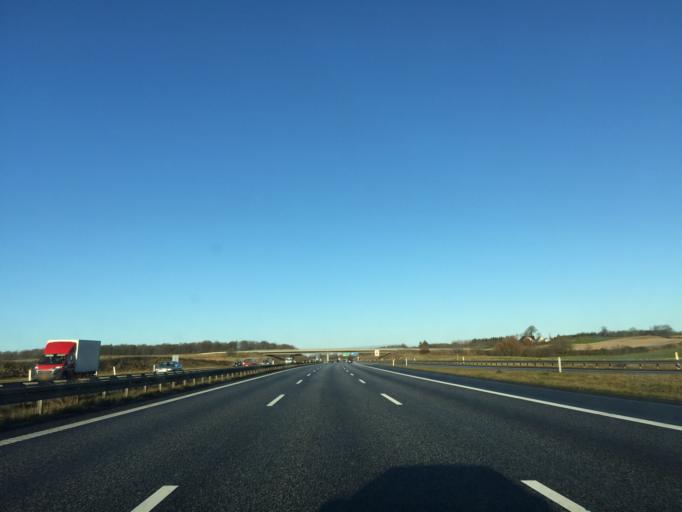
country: DK
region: South Denmark
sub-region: Vejle Kommune
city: Vejle
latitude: 55.6443
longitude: 9.5608
